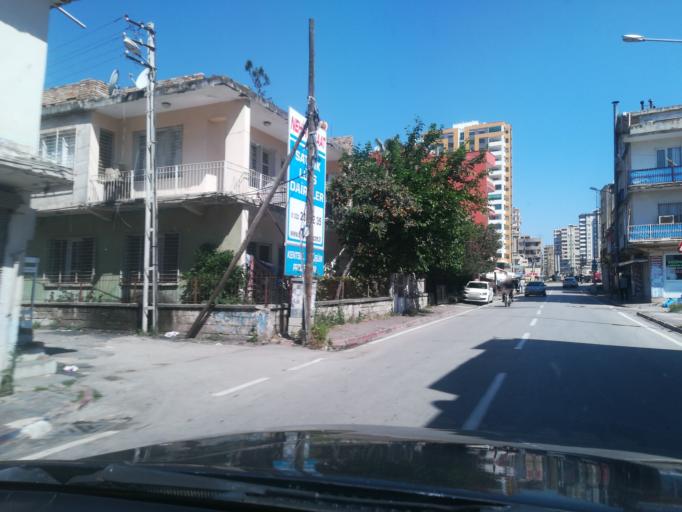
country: TR
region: Adana
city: Adana
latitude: 37.0085
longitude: 35.3210
